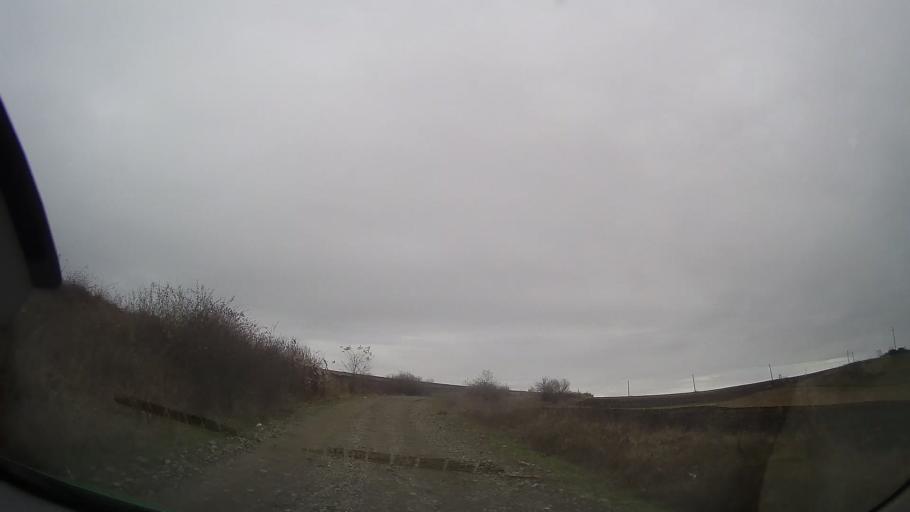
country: RO
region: Mures
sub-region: Comuna Bala
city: Bala
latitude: 46.6982
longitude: 24.4913
